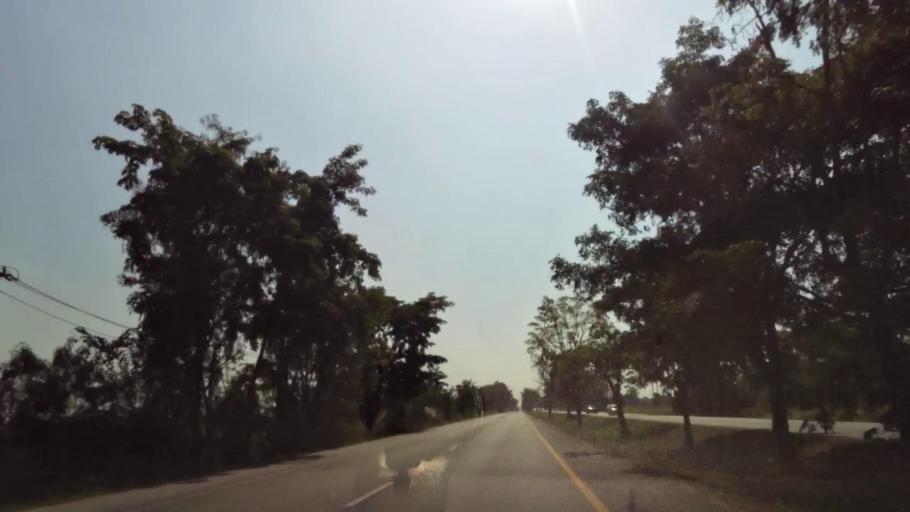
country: TH
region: Phichit
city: Bueng Na Rang
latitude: 16.2853
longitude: 100.1276
